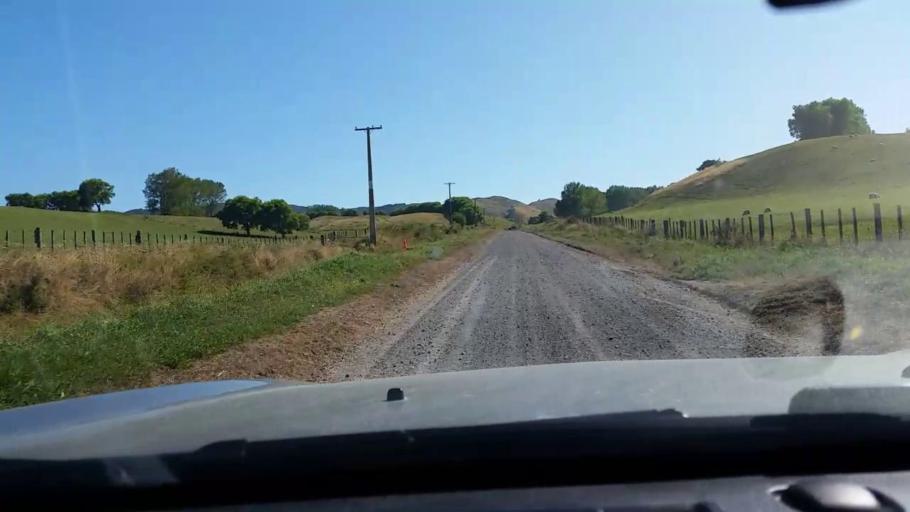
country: NZ
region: Bay of Plenty
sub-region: Rotorua District
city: Rotorua
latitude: -38.3210
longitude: 176.2975
